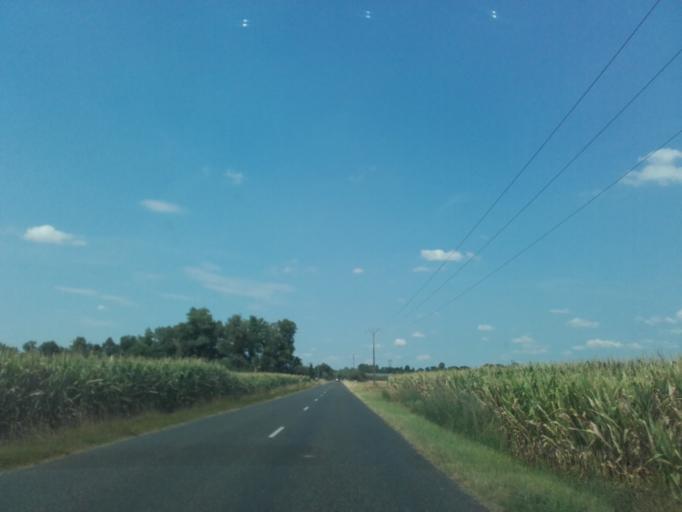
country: FR
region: Rhone-Alpes
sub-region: Departement de l'Ain
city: Saint-Maurice-de-Gourdans
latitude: 45.8035
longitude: 5.2128
